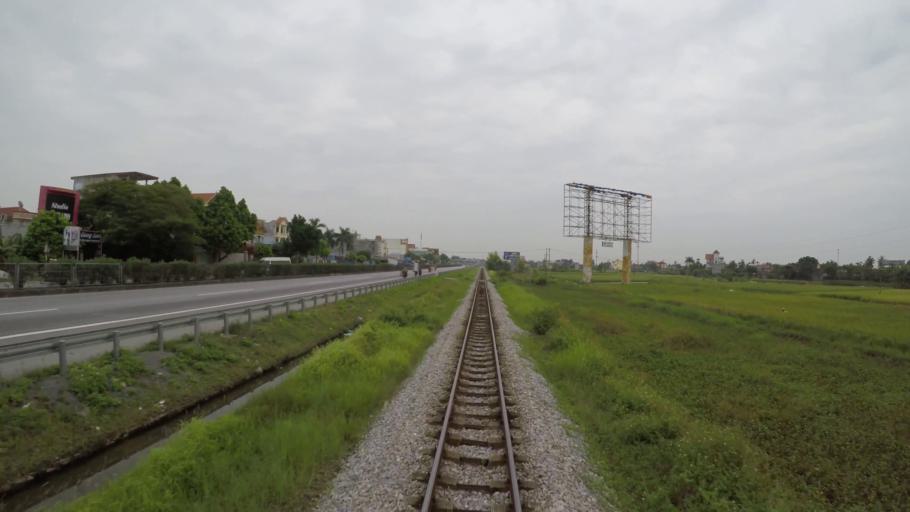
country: VN
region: Hai Duong
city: Phu Thai
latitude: 20.9295
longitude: 106.5545
